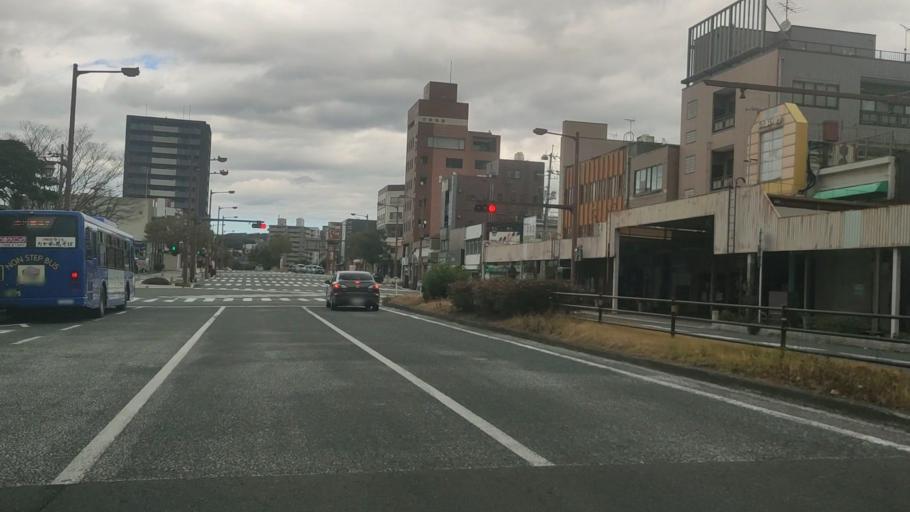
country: JP
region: Yamaguchi
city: Shimonoseki
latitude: 33.9574
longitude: 130.9425
